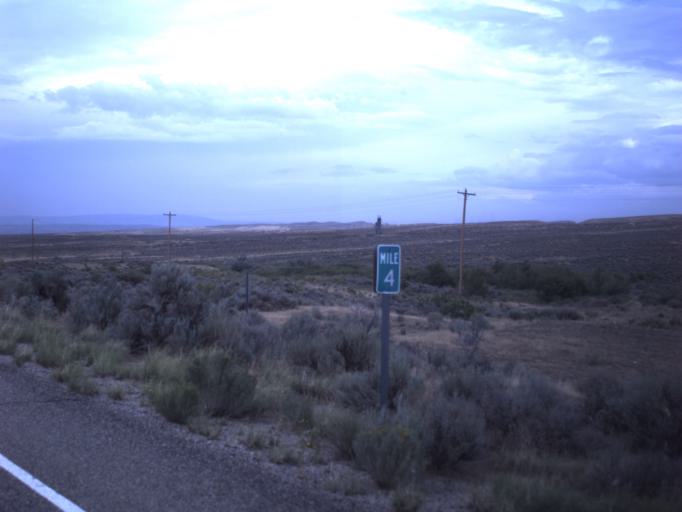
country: US
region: Colorado
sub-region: Rio Blanco County
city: Rangely
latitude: 40.0071
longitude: -109.1690
